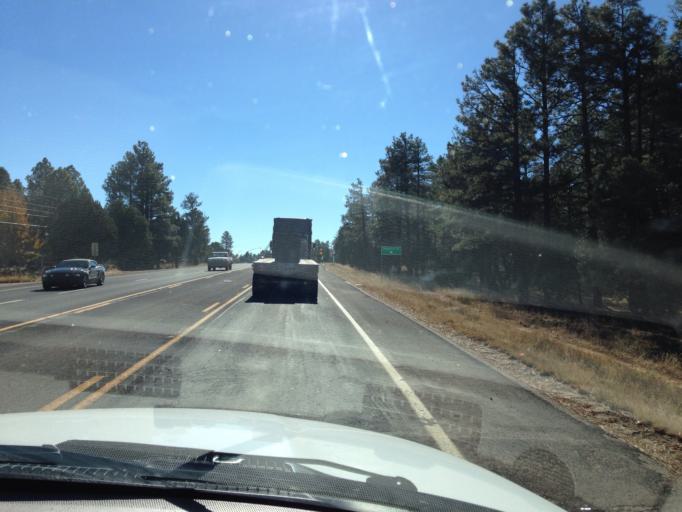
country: US
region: Arizona
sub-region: Navajo County
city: Show Low
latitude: 34.2591
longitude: -110.0882
